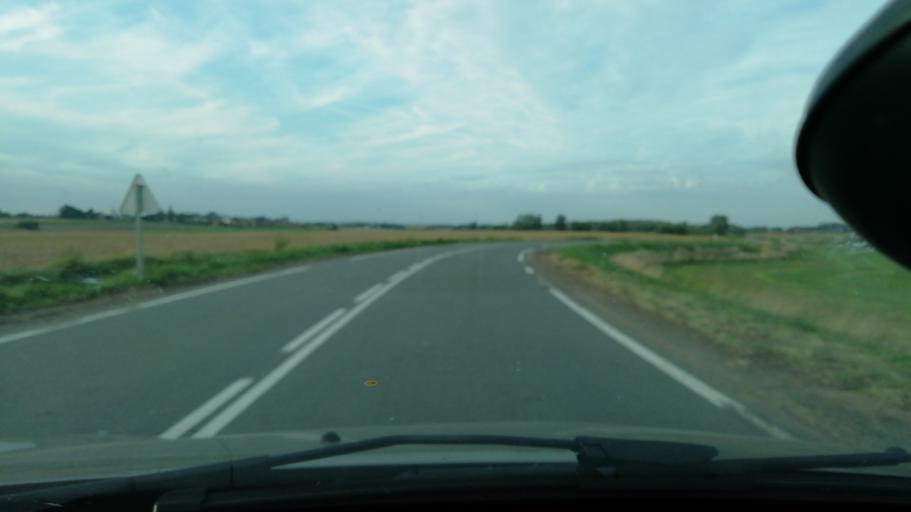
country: FR
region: Nord-Pas-de-Calais
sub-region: Departement du Nord
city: Caudry
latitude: 50.1234
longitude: 3.4406
